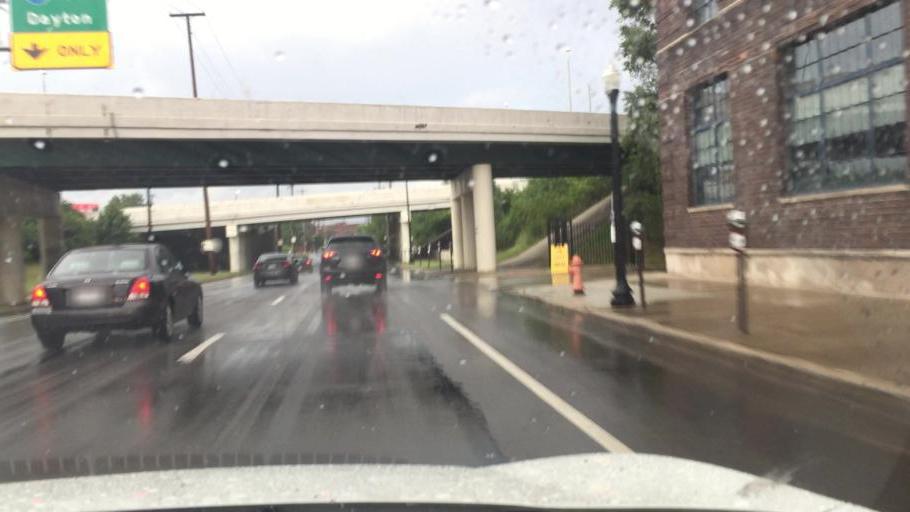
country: US
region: Ohio
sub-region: Franklin County
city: Columbus
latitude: 39.9749
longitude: -82.9982
